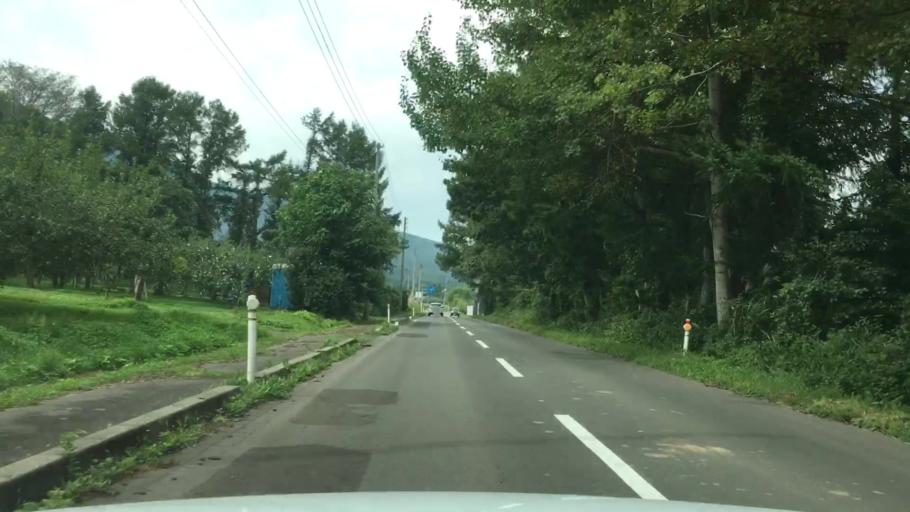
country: JP
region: Aomori
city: Hirosaki
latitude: 40.6776
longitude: 140.3767
